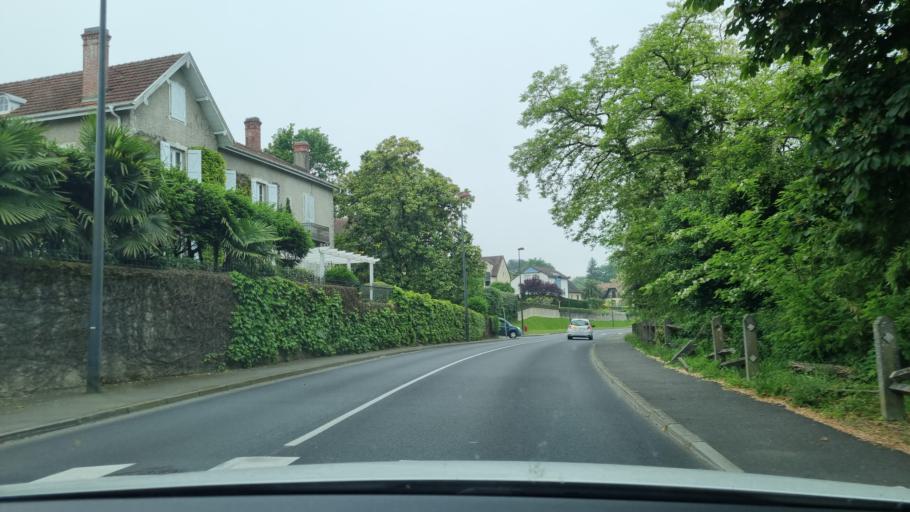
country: FR
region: Aquitaine
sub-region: Departement des Pyrenees-Atlantiques
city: Orthez
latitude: 43.4823
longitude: -0.7687
